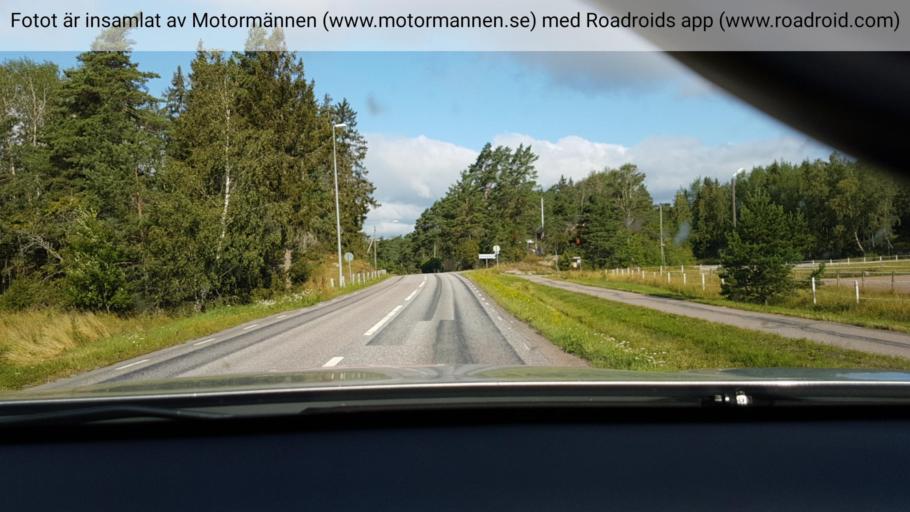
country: SE
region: Stockholm
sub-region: Norrtalje Kommun
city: Nykvarn
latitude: 59.8703
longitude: 18.0668
